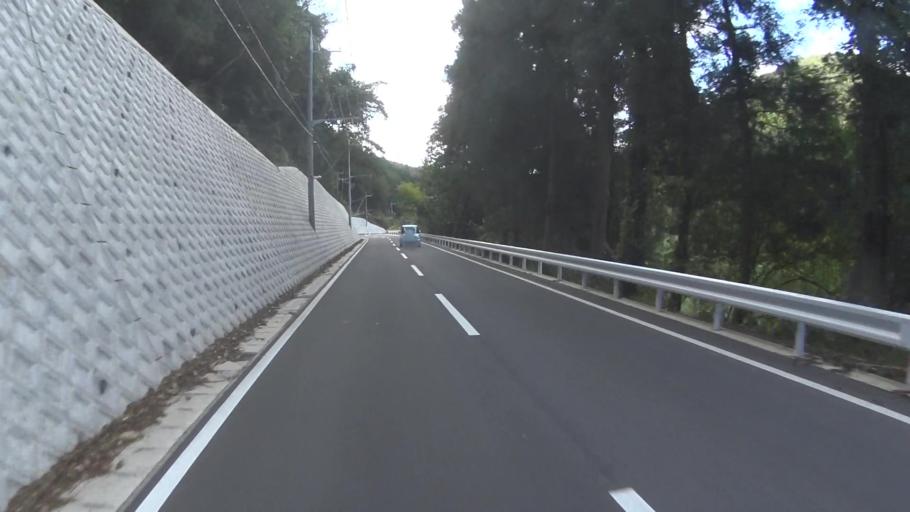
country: JP
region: Kyoto
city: Maizuru
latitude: 35.5572
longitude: 135.4367
